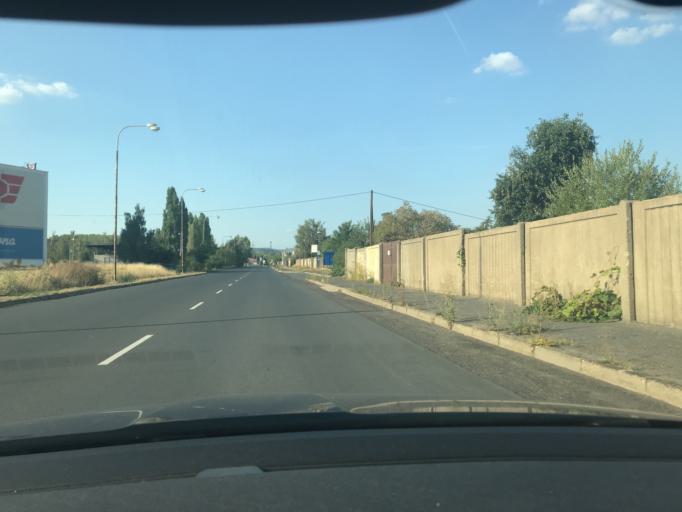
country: CZ
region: Ustecky
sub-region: Okres Chomutov
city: Chomutov
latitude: 50.4454
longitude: 13.3972
